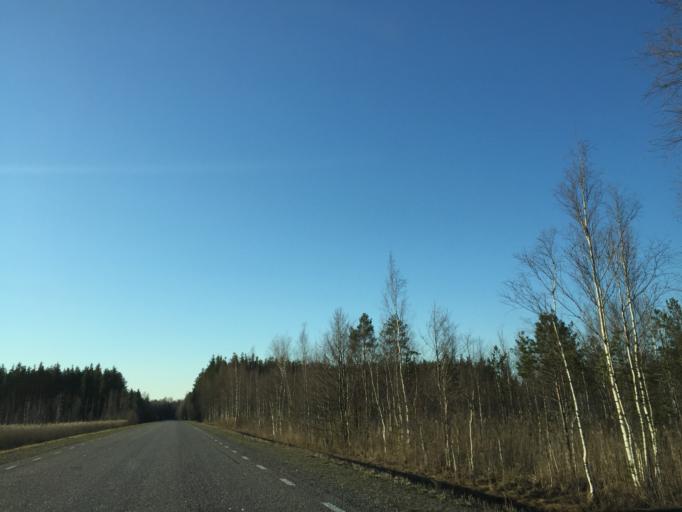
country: EE
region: Ida-Virumaa
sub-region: Toila vald
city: Voka
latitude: 59.1176
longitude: 27.6325
